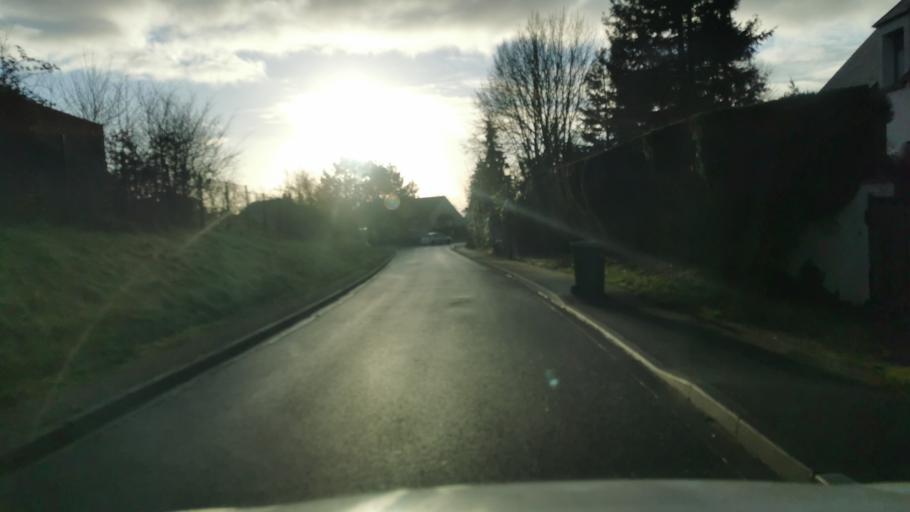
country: FR
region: Ile-de-France
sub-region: Departement des Yvelines
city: Bazainville
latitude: 48.8257
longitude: 1.6337
